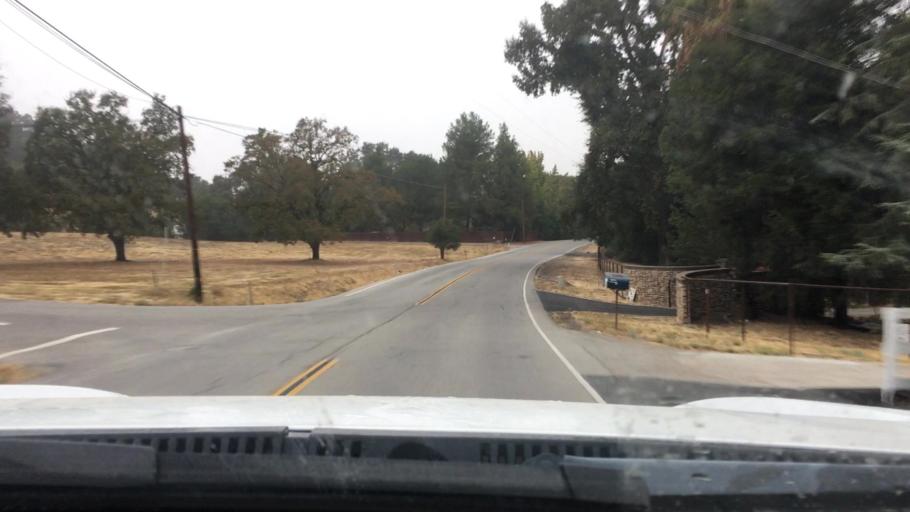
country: US
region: California
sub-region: San Luis Obispo County
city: Atascadero
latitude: 35.4925
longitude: -120.6846
